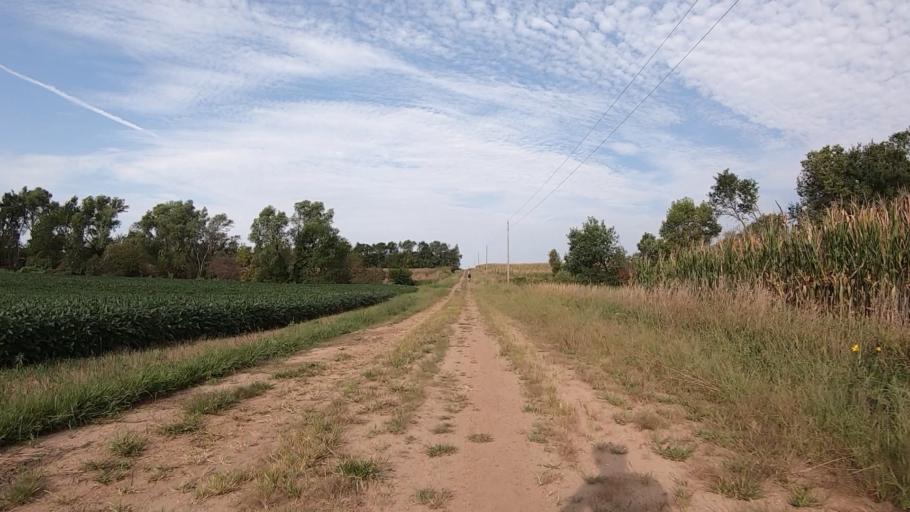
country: US
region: Kansas
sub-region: Washington County
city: Washington
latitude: 39.6750
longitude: -96.9495
